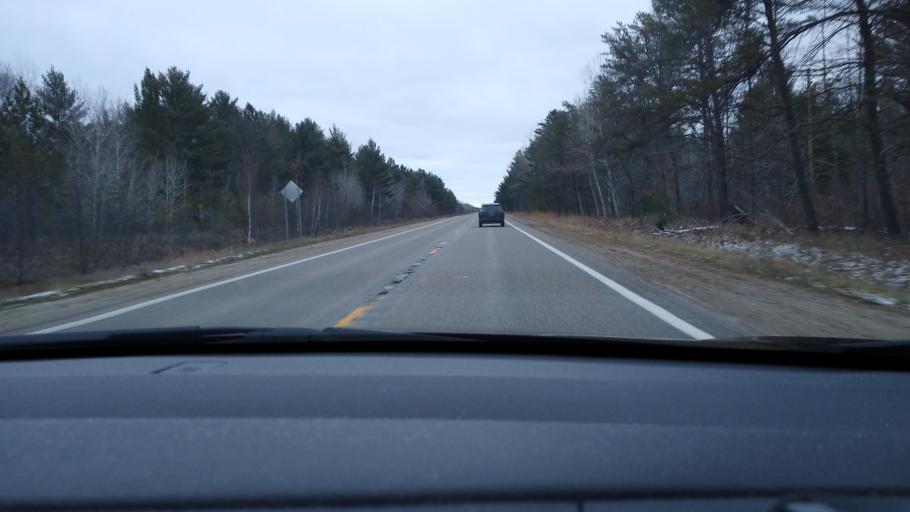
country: US
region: Michigan
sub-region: Roscommon County
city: Houghton Lake
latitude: 44.3358
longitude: -84.8671
